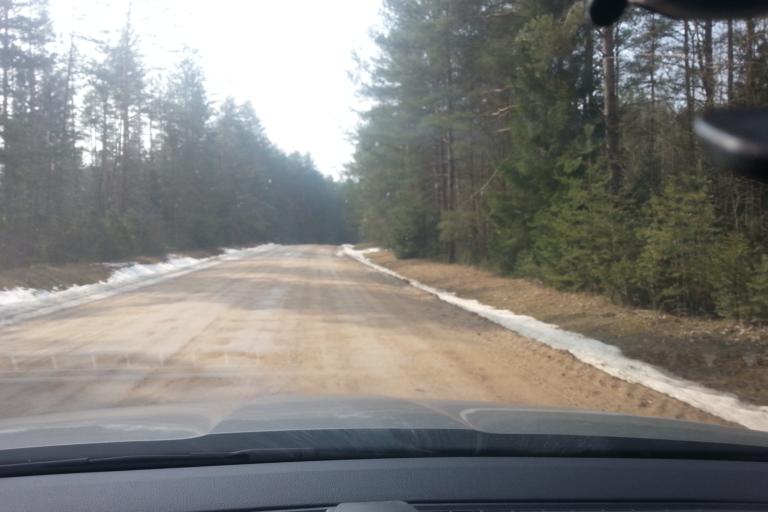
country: LT
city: Trakai
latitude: 54.5256
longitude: 24.9645
